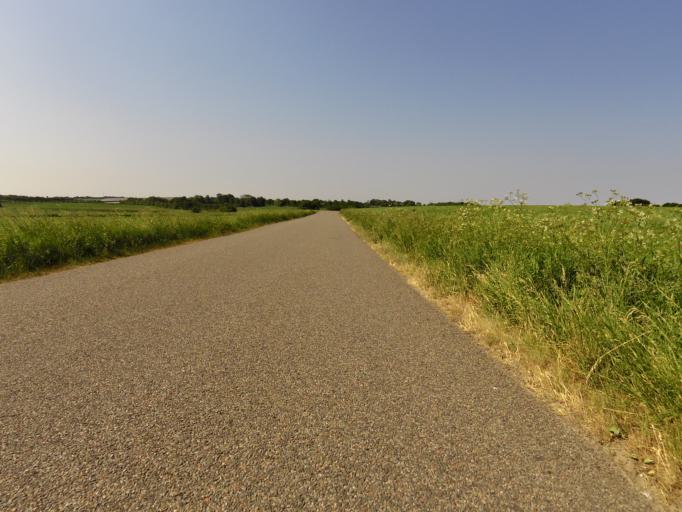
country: DK
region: Central Jutland
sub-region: Holstebro Kommune
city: Vinderup
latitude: 56.4774
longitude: 8.8243
